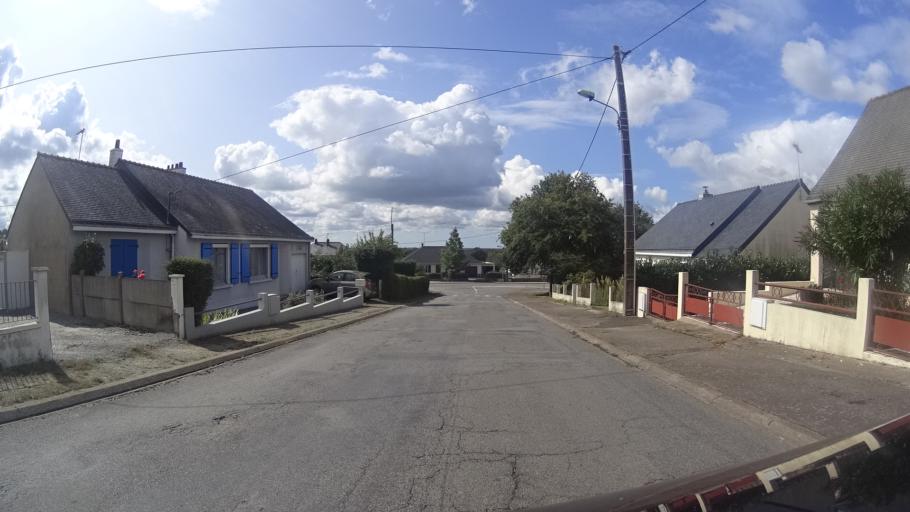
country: FR
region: Pays de la Loire
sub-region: Departement de la Loire-Atlantique
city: Savenay
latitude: 47.3550
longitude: -1.9397
